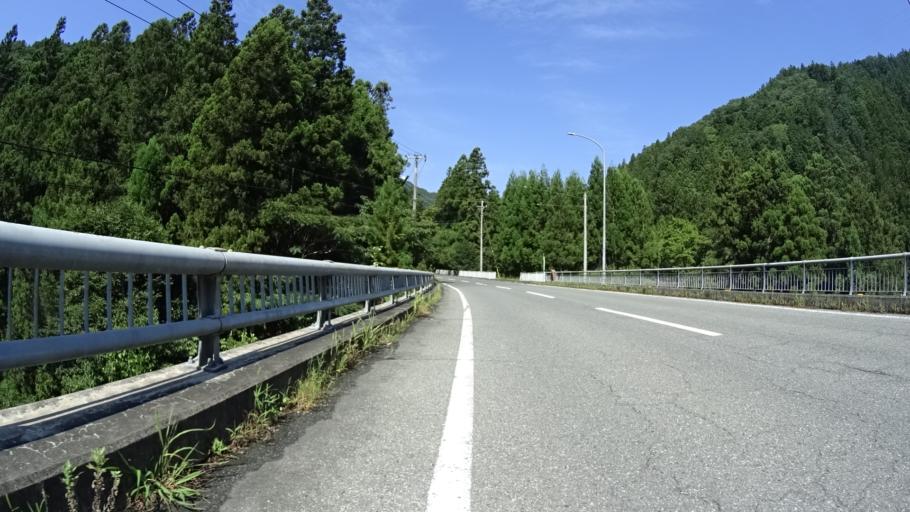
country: JP
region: Saitama
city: Chichibu
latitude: 36.0276
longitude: 138.9484
